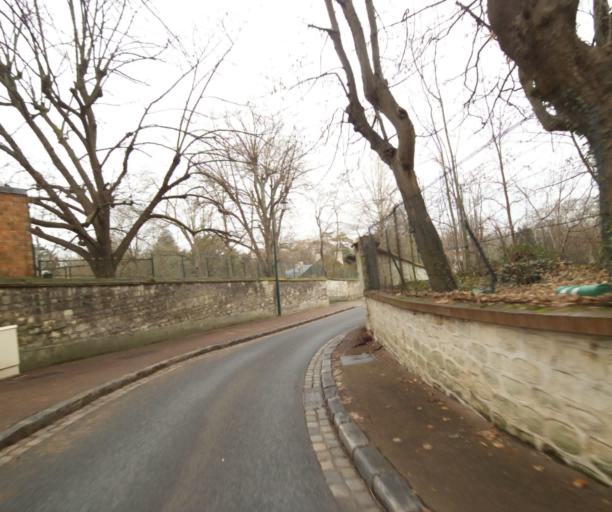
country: FR
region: Ile-de-France
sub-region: Departement des Hauts-de-Seine
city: Rueil-Malmaison
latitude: 48.8695
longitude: 2.1701
